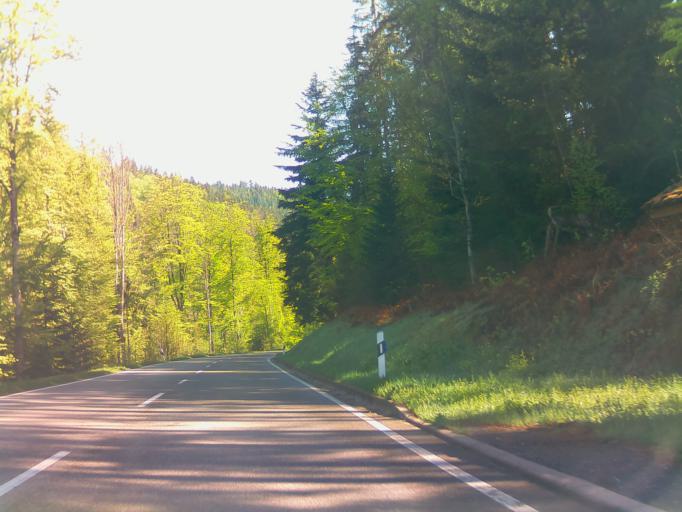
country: DE
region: Baden-Wuerttemberg
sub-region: Karlsruhe Region
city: Bad Wildbad
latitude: 48.7180
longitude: 8.5616
